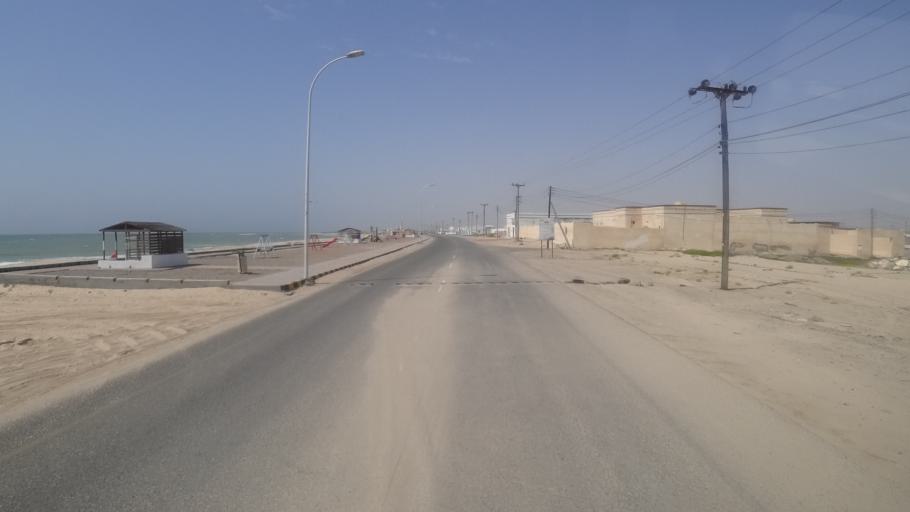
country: OM
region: Ash Sharqiyah
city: Sur
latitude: 22.1160
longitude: 59.7134
